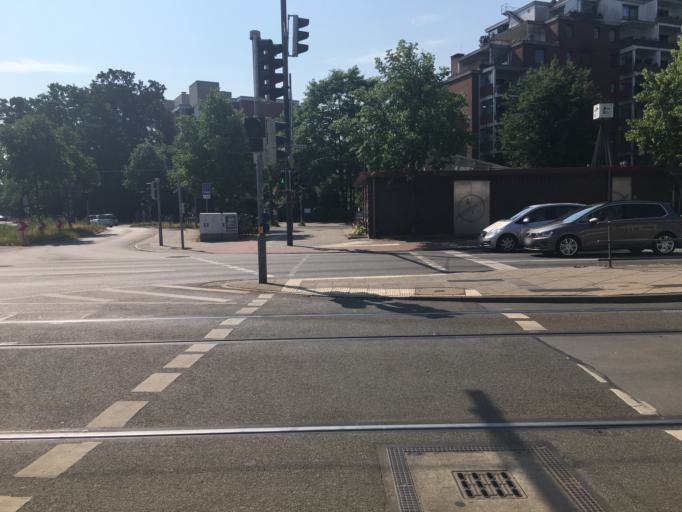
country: DE
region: Lower Saxony
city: Lilienthal
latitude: 53.1017
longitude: 8.8803
